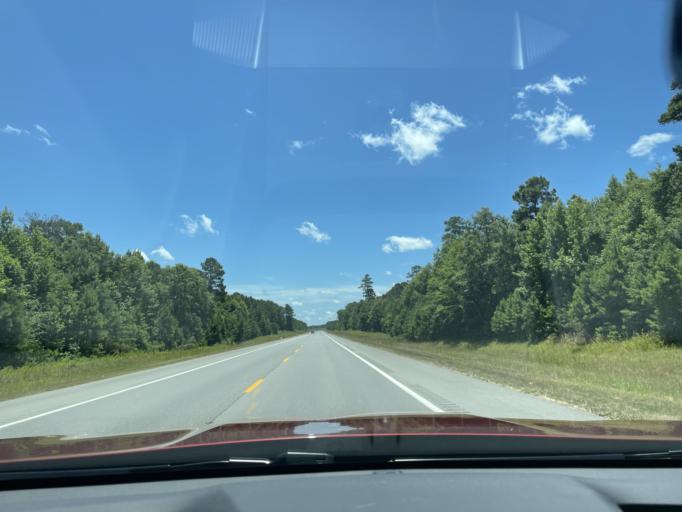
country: US
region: Arkansas
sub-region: Lincoln County
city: Star City
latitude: 33.9703
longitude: -91.9148
